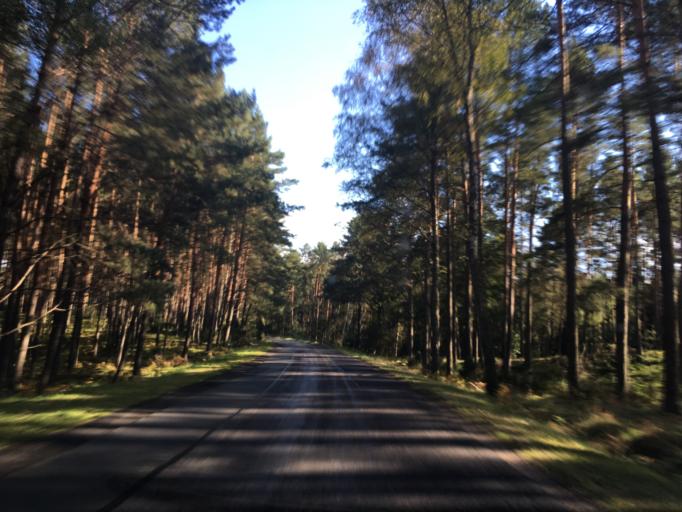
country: PL
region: Kujawsko-Pomorskie
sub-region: Powiat swiecki
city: Warlubie
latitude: 53.6047
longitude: 18.5522
